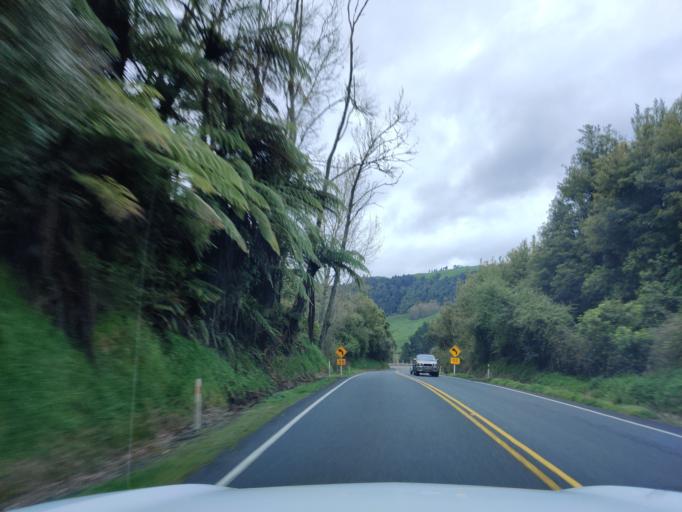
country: NZ
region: Waikato
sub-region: Otorohanga District
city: Otorohanga
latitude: -38.4940
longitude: 175.1889
